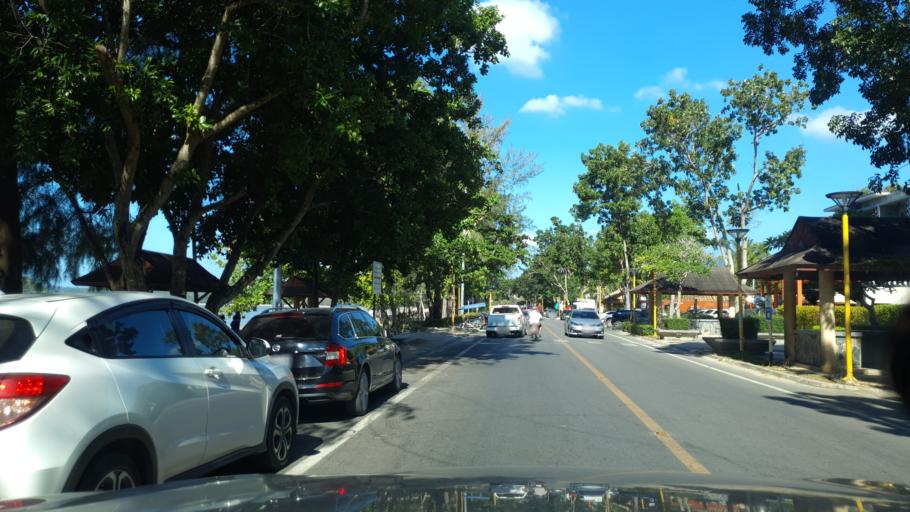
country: TH
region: Phangnga
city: Ban Ao Nang
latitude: 8.0408
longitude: 98.8136
